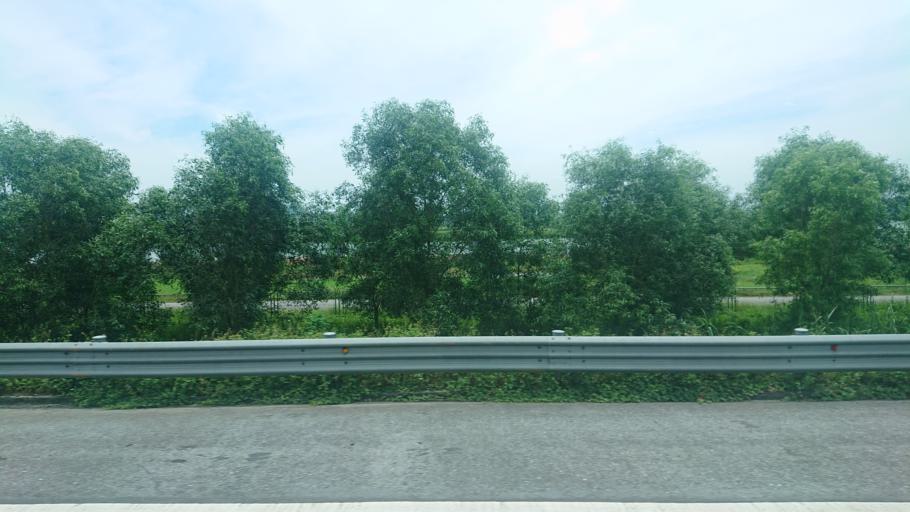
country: VN
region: Hai Phong
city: An Lao
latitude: 20.7800
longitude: 106.5705
